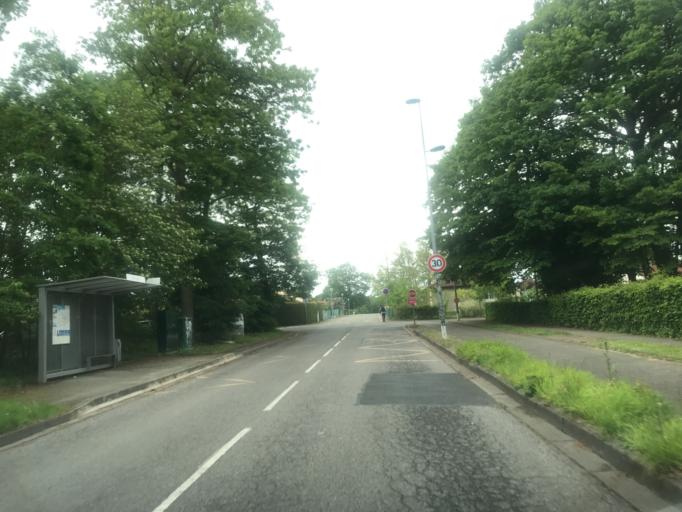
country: FR
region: Haute-Normandie
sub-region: Departement de l'Eure
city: Evreux
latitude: 49.0100
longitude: 1.1382
